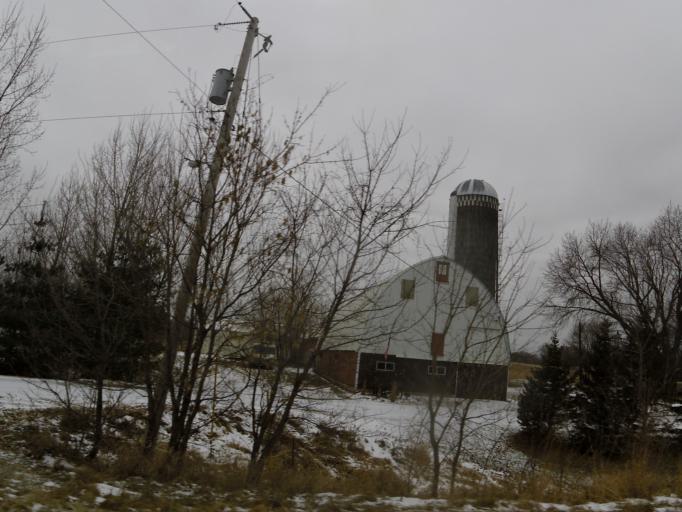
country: US
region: Minnesota
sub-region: Wright County
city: Montrose
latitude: 45.0593
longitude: -93.8589
